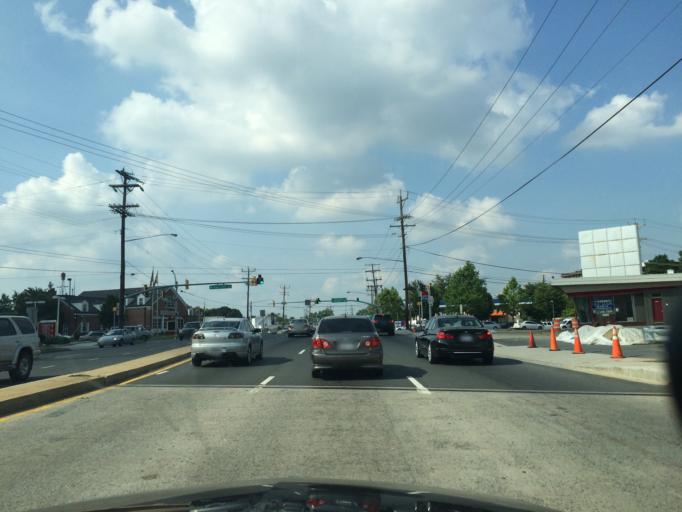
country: US
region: Maryland
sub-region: Montgomery County
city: Kensington
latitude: 39.0289
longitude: -77.0760
